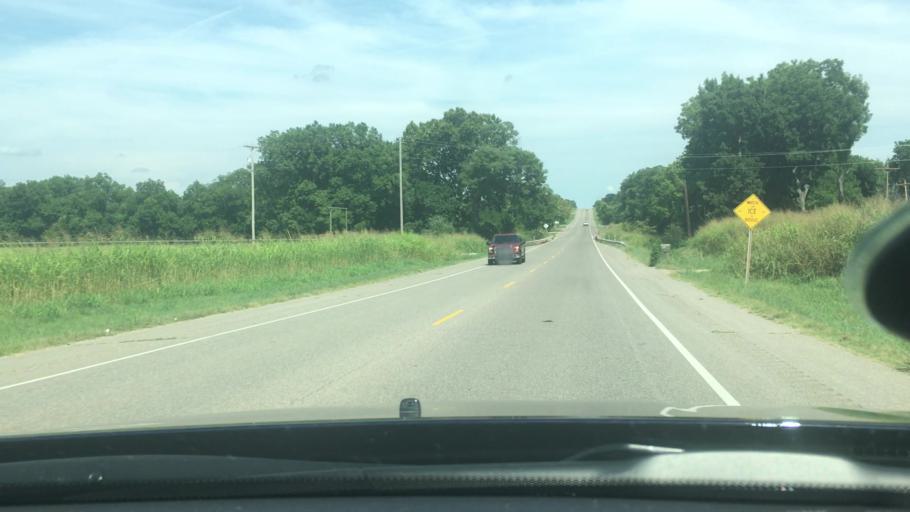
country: US
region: Oklahoma
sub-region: Pottawatomie County
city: Shawnee
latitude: 35.3331
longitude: -96.8466
